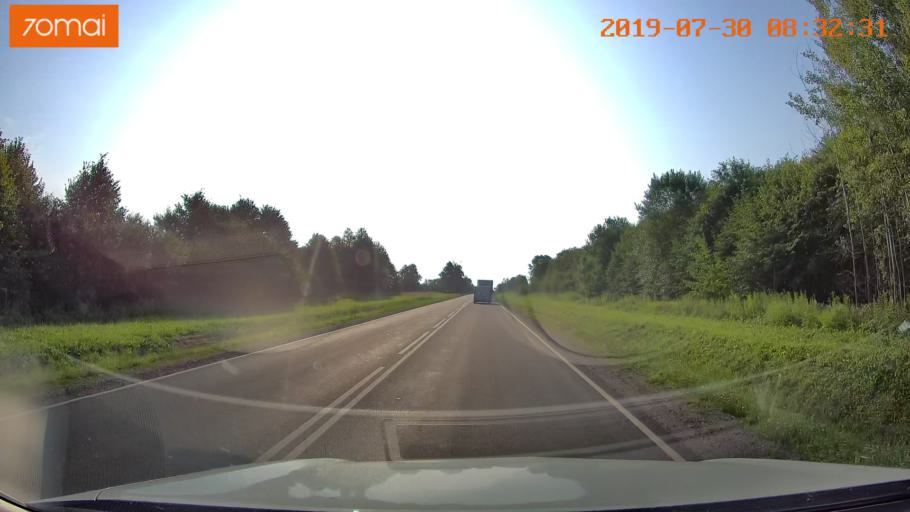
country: RU
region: Kaliningrad
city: Chernyakhovsk
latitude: 54.6376
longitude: 21.7299
